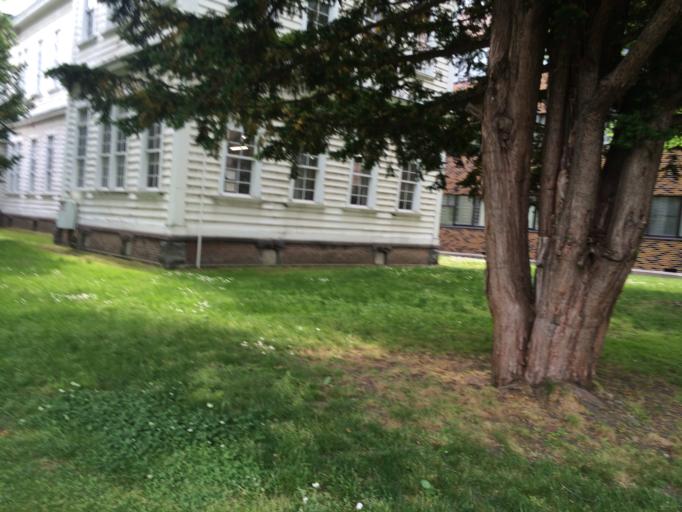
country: JP
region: Hokkaido
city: Sapporo
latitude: 43.0713
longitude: 141.3440
